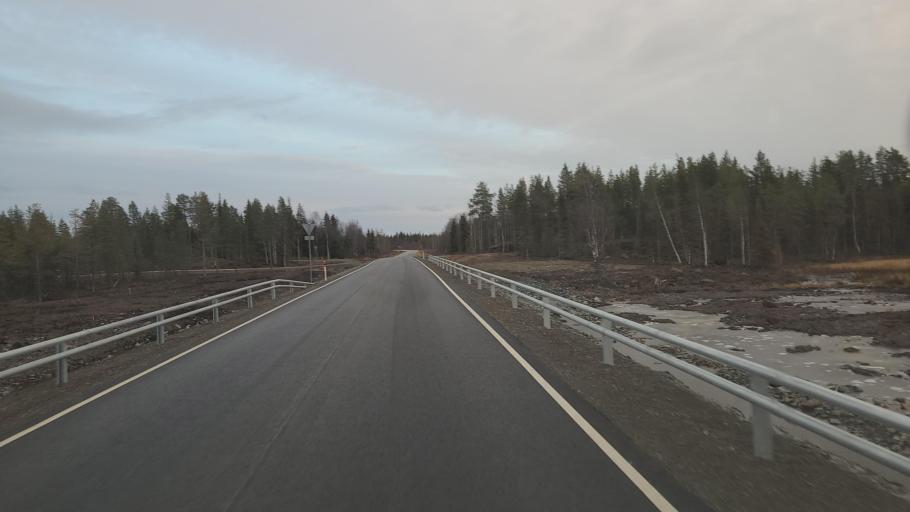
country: FI
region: Lapland
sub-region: Tunturi-Lappi
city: Kittilae
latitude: 67.9040
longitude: 25.0824
